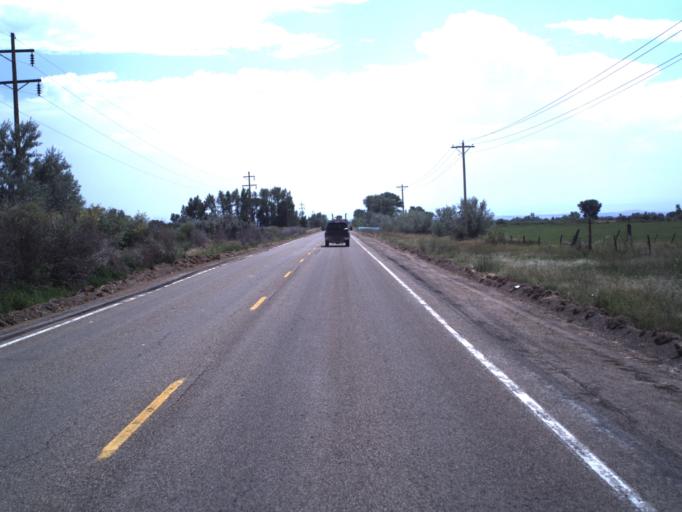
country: US
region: Utah
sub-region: Duchesne County
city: Roosevelt
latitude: 40.4004
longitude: -110.0299
